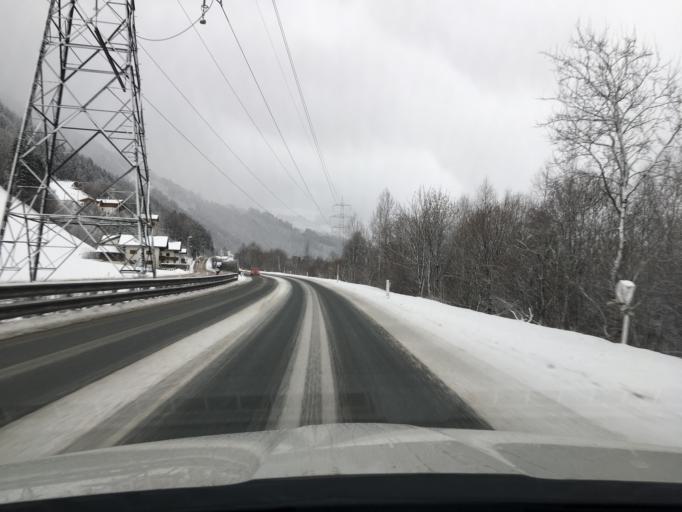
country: AT
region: Tyrol
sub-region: Politischer Bezirk Schwaz
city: Rohrberg
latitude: 47.2490
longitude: 11.9015
